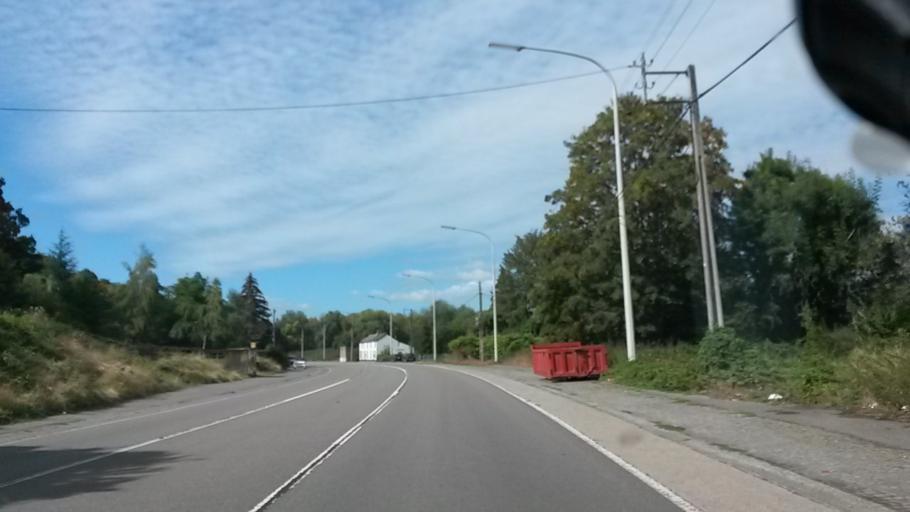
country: BE
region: Wallonia
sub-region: Province de Liege
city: Wanze
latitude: 50.5248
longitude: 5.2028
